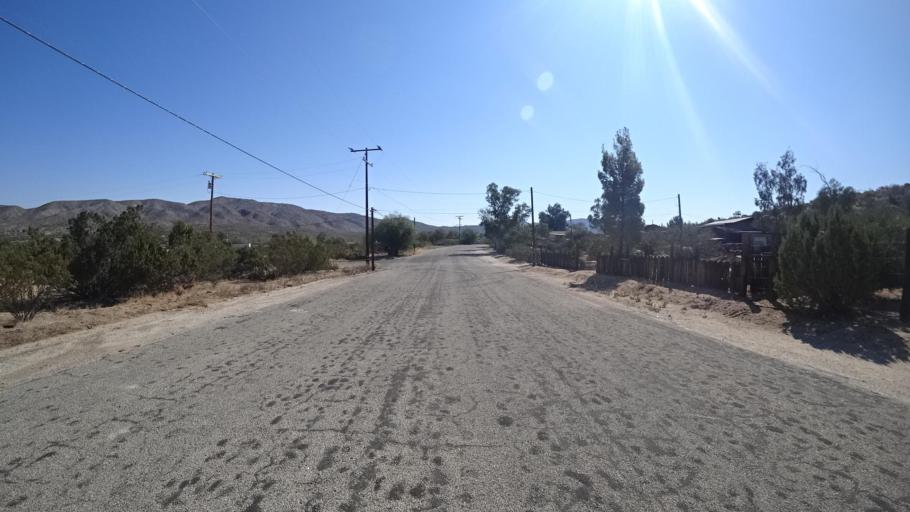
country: US
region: California
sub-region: San Diego County
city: Julian
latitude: 33.0747
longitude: -116.4450
